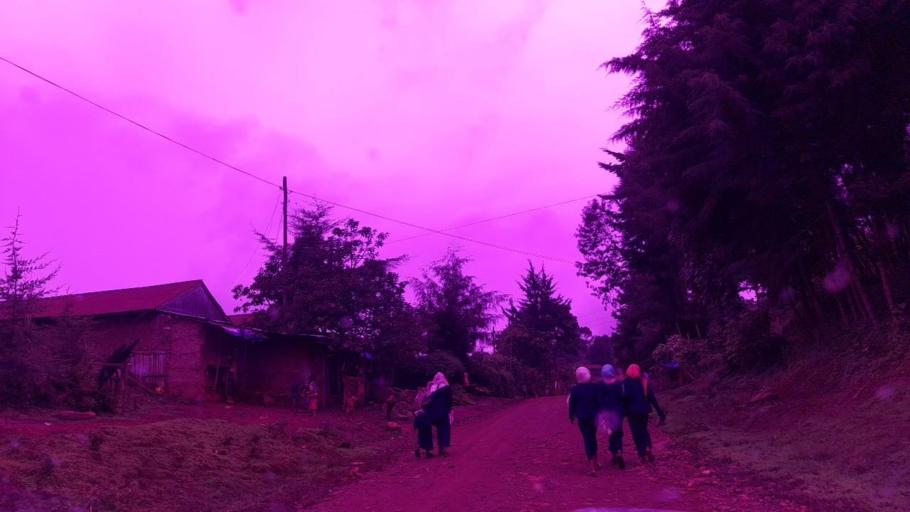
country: ET
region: Southern Nations, Nationalities, and People's Region
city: Tippi
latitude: 7.5918
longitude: 35.7648
